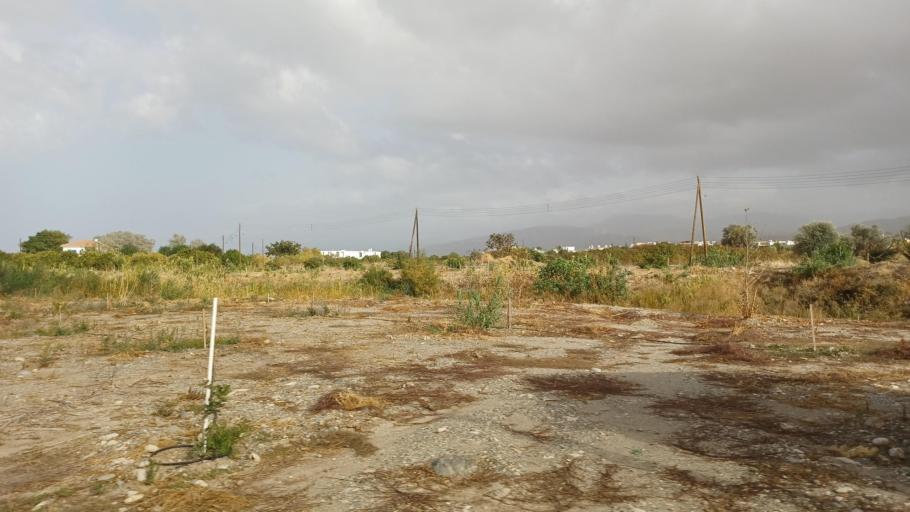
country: CY
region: Pafos
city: Polis
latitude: 35.0415
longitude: 32.4229
